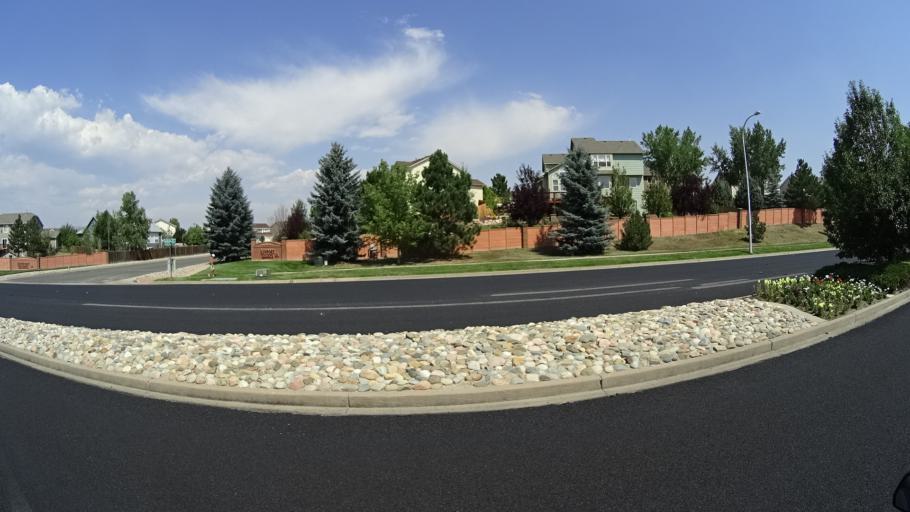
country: US
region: Colorado
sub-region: El Paso County
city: Cimarron Hills
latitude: 38.9315
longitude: -104.7454
